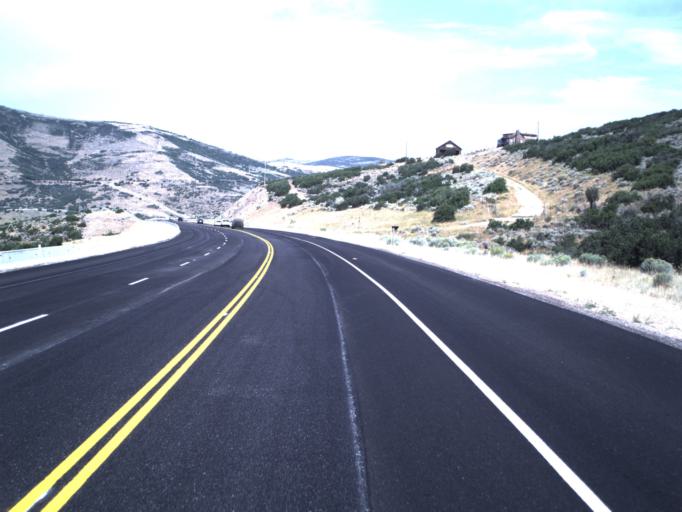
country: US
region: Utah
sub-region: Summit County
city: Park City
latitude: 40.6489
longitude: -111.4023
